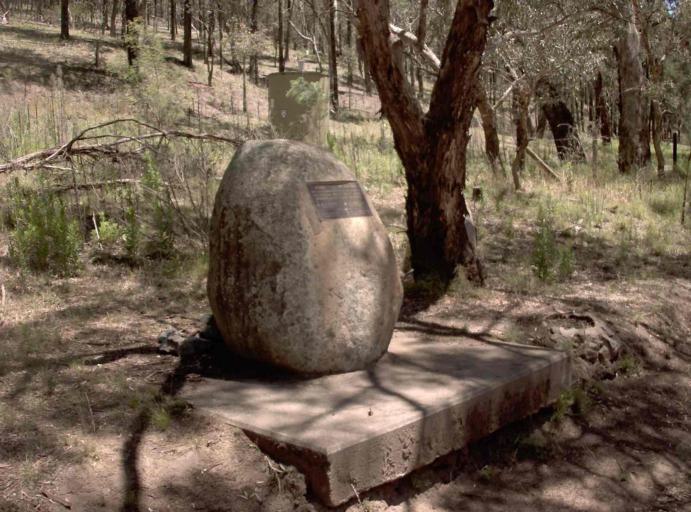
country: AU
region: New South Wales
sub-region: Snowy River
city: Jindabyne
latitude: -36.8882
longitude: 148.4206
